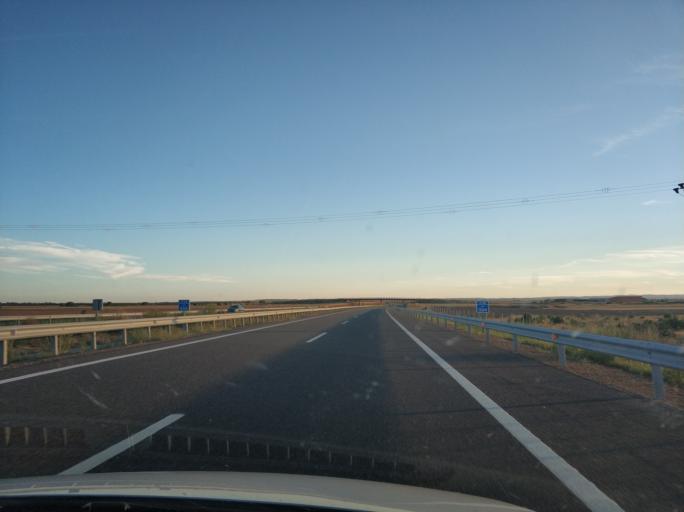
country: ES
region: Castille and Leon
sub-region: Provincia de Zamora
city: Barcial del Barco
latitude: 41.9324
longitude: -5.6492
